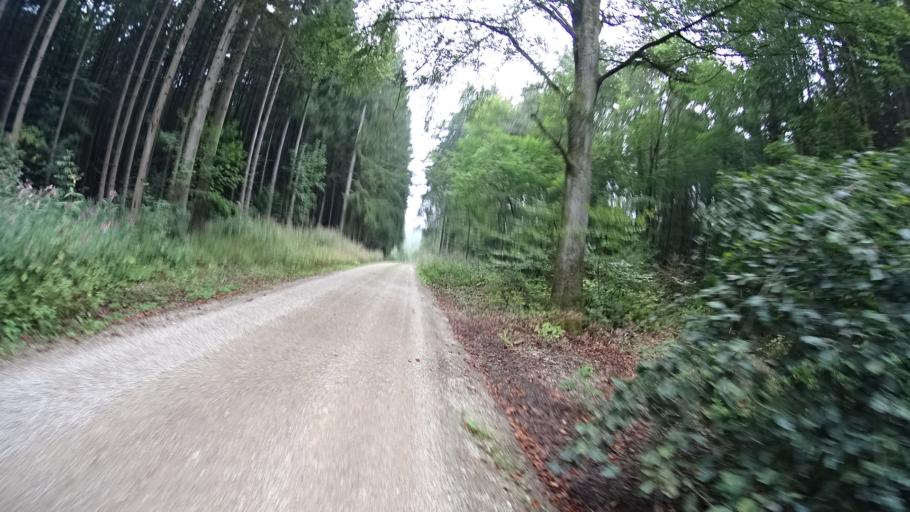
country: DE
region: Bavaria
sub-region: Upper Bavaria
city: Stammham
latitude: 48.8598
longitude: 11.4977
